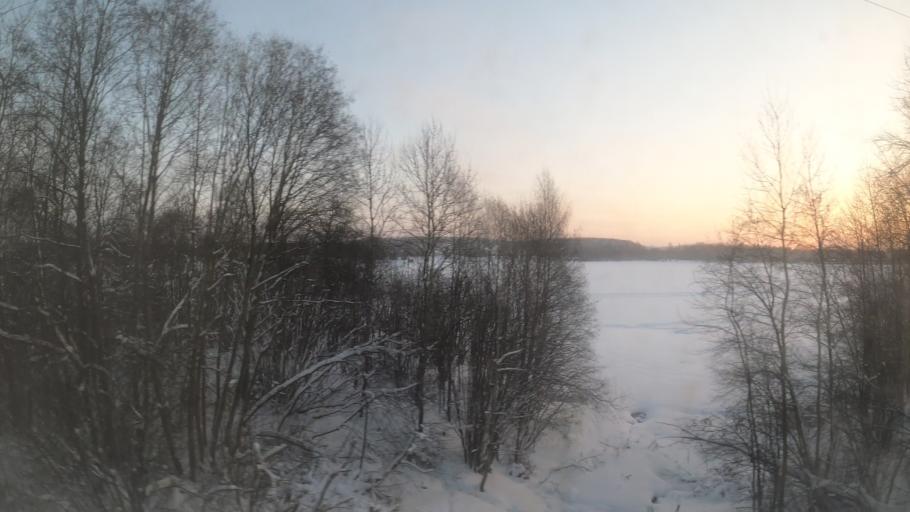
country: RU
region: Moskovskaya
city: Yermolino
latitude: 56.1506
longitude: 37.5043
